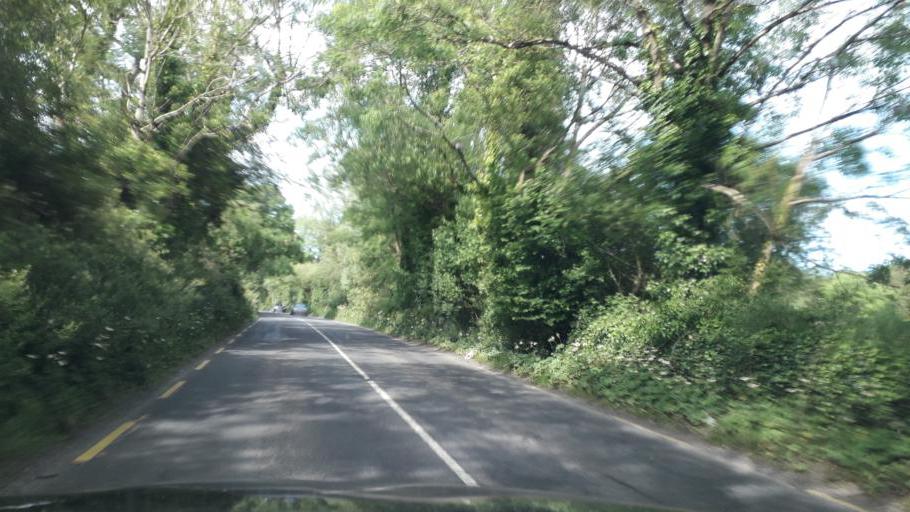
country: IE
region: Leinster
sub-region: Loch Garman
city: Castlebridge
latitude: 52.4110
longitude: -6.4234
